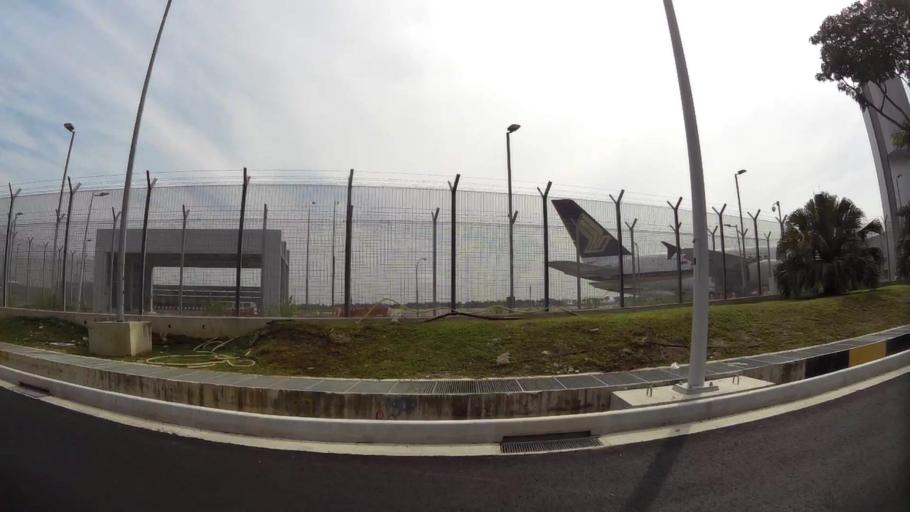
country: SG
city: Singapore
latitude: 1.3436
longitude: 103.9838
